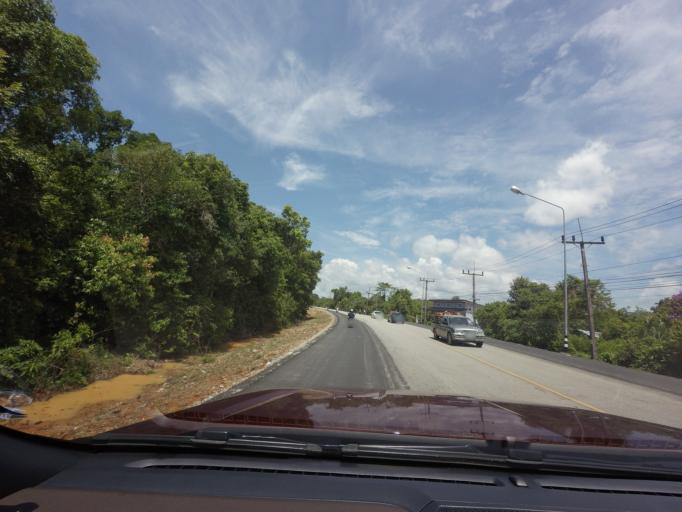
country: TH
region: Narathiwat
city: Ra-ngae
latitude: 6.2830
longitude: 101.7011
